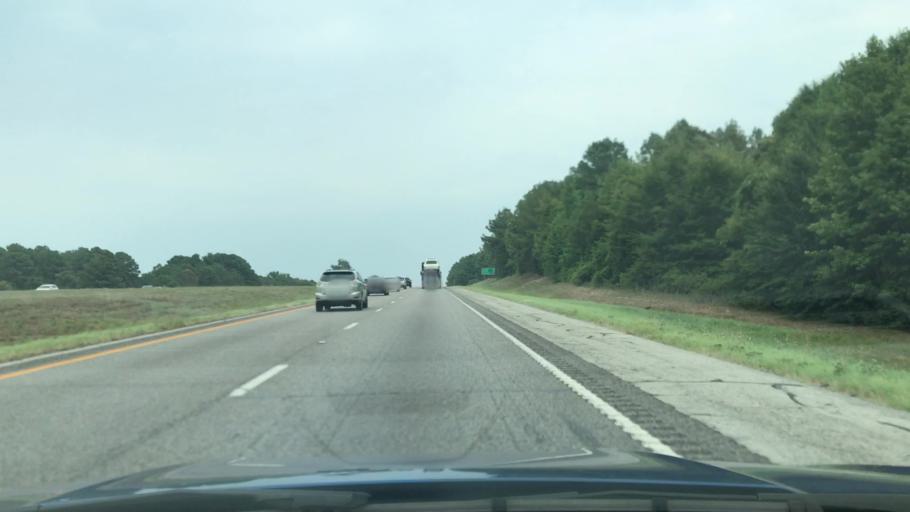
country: US
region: Texas
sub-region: Smith County
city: Lindale
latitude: 32.4684
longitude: -95.3563
